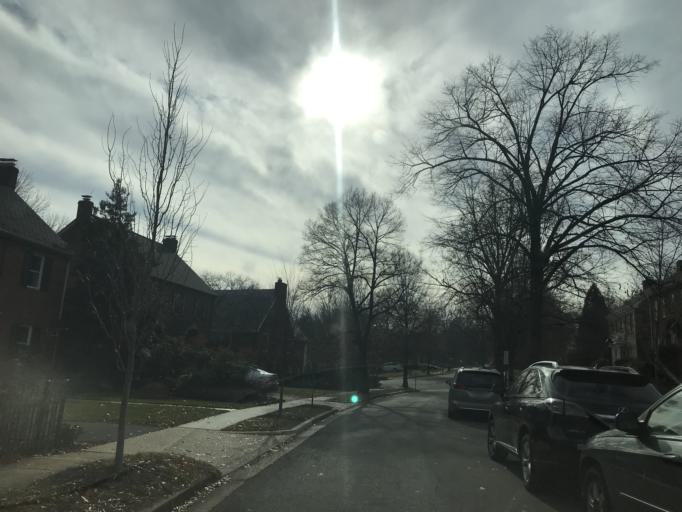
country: US
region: Virginia
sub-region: Arlington County
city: Arlington
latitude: 38.8938
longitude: -77.0955
